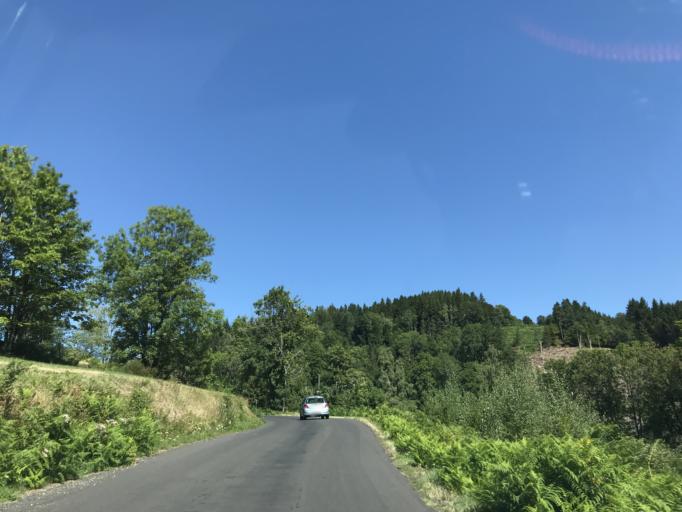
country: FR
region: Auvergne
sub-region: Departement du Puy-de-Dome
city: Job
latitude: 45.6717
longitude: 3.7462
